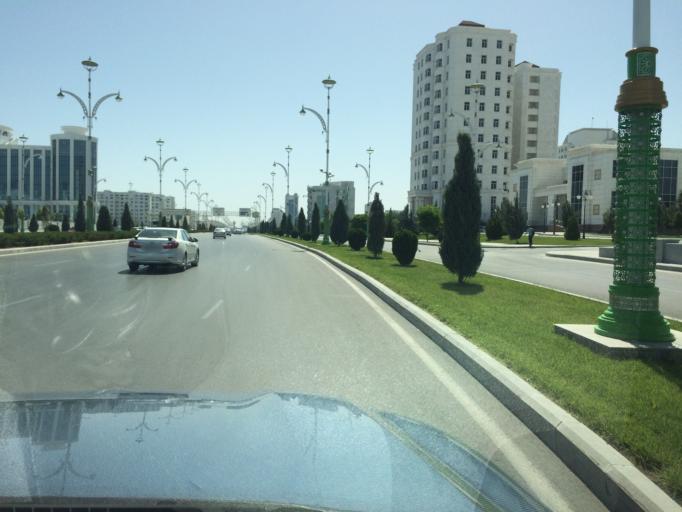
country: TM
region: Ahal
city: Ashgabat
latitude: 37.8956
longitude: 58.3741
